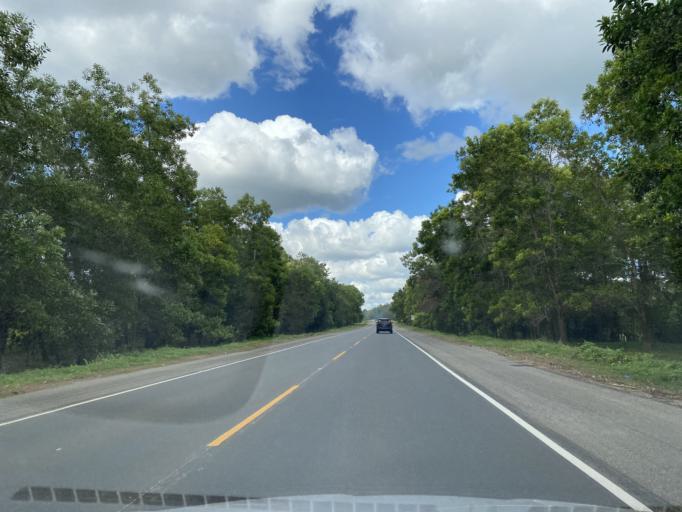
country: DO
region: Monte Plata
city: Monte Plata
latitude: 18.6876
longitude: -69.7483
